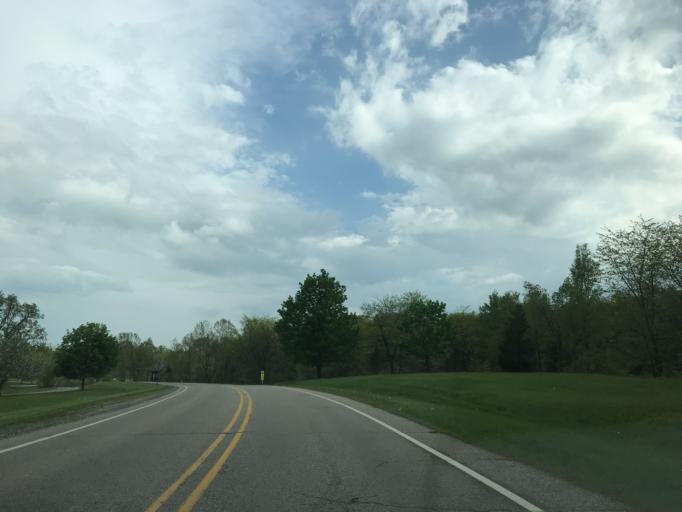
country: US
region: Michigan
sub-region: Oakland County
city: Milford
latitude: 42.5454
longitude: -83.6406
